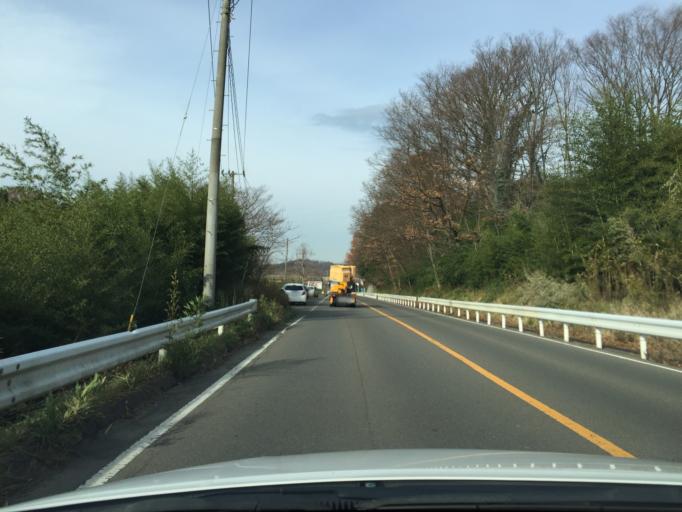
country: JP
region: Fukushima
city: Fukushima-shi
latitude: 37.6733
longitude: 140.4664
